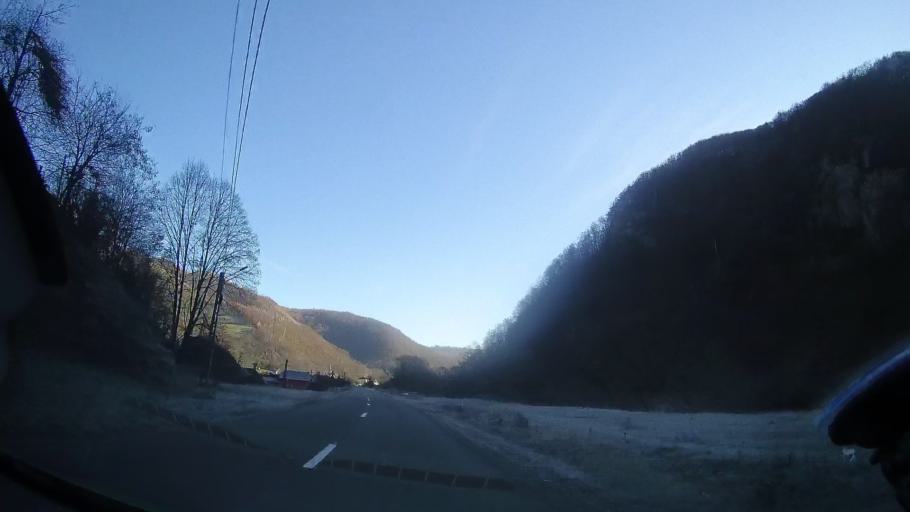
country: RO
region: Bihor
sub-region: Comuna Bulz
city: Bulz
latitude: 46.9147
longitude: 22.6666
